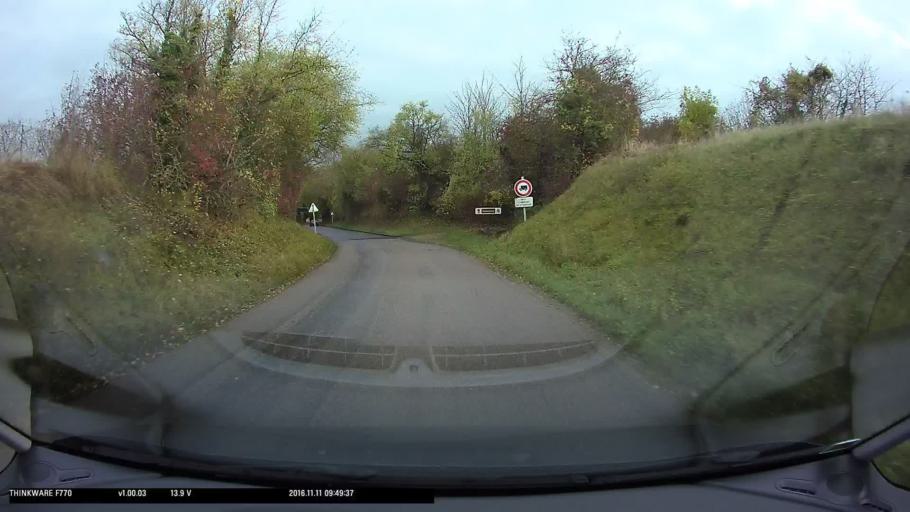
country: FR
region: Ile-de-France
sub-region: Departement du Val-d'Oise
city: Ableiges
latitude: 49.0717
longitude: 2.0051
